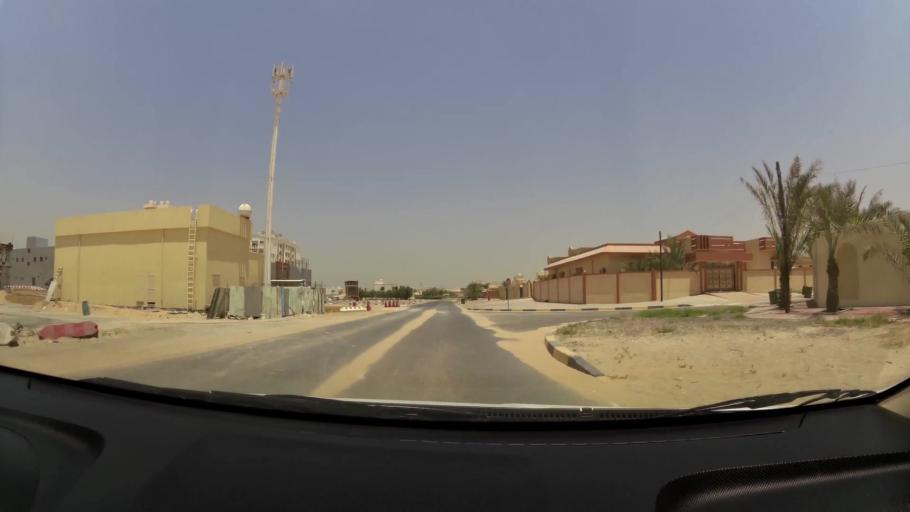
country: AE
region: Ajman
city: Ajman
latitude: 25.4099
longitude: 55.5189
